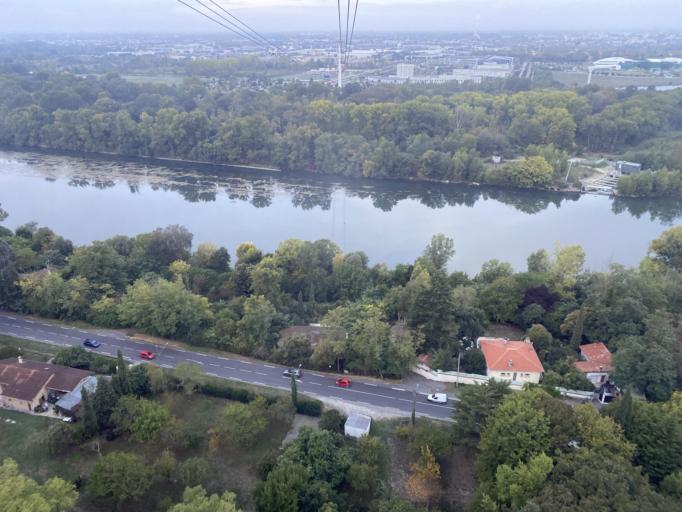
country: FR
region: Midi-Pyrenees
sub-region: Departement de la Haute-Garonne
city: Vieille-Toulouse
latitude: 43.5566
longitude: 1.4424
